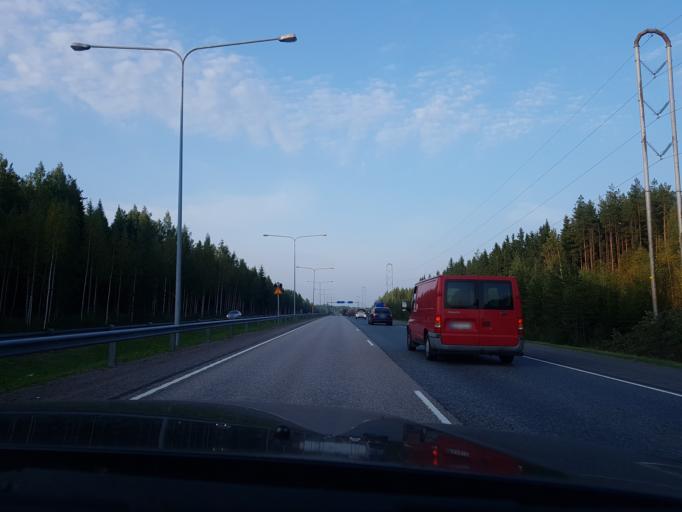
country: FI
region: Uusimaa
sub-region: Helsinki
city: Tuusula
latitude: 60.3629
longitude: 25.0041
